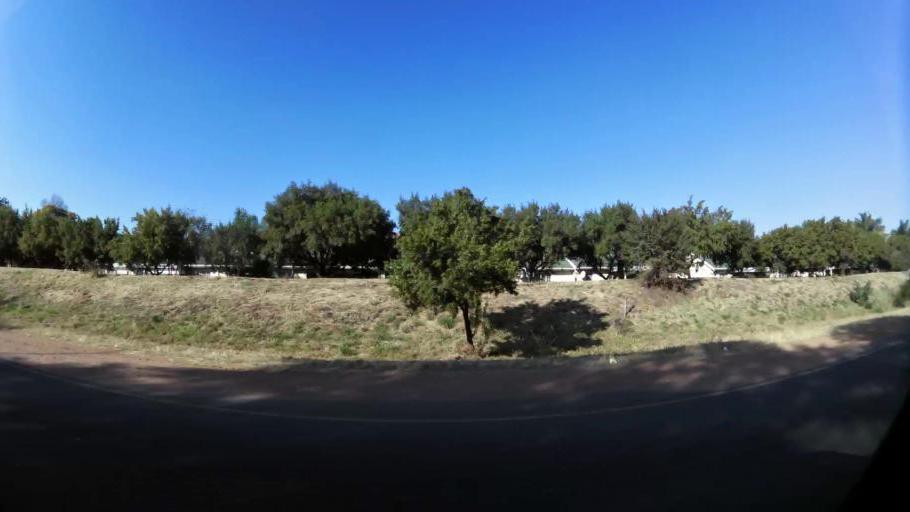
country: ZA
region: Gauteng
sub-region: City of Tshwane Metropolitan Municipality
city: Pretoria
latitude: -25.6775
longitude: 28.1417
